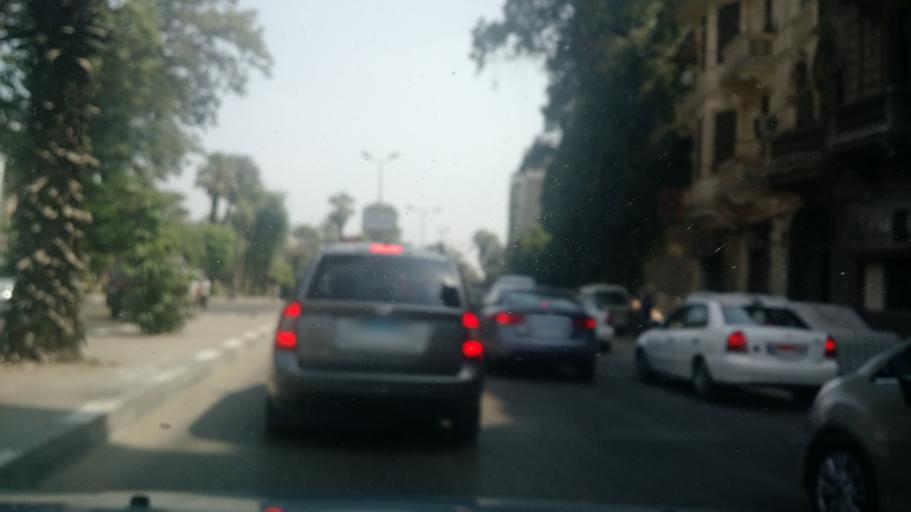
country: EG
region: Al Jizah
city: Al Jizah
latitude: 30.0060
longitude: 31.2264
